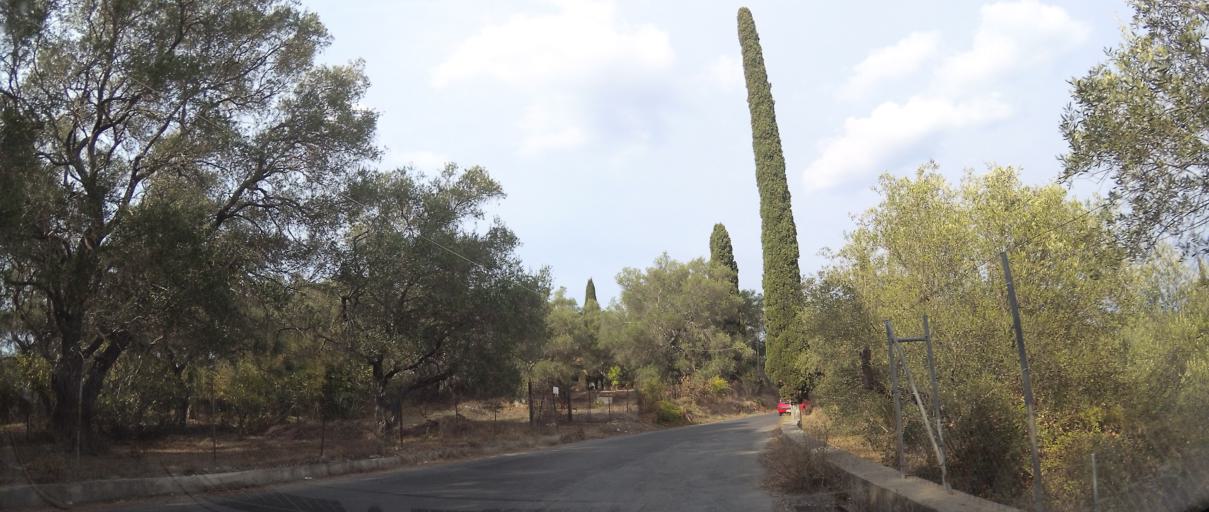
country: GR
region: Ionian Islands
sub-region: Nomos Kerkyras
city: Kynopiastes
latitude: 39.5588
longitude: 19.8614
